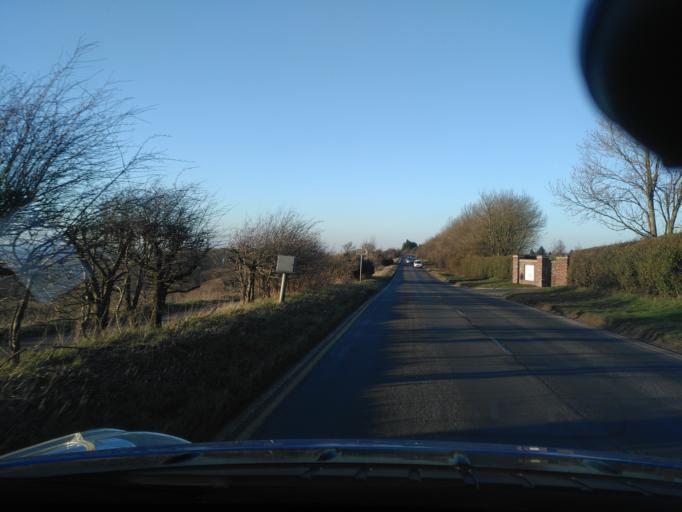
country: GB
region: England
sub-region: Central Bedfordshire
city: Dunstable
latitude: 51.8719
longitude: -0.5369
